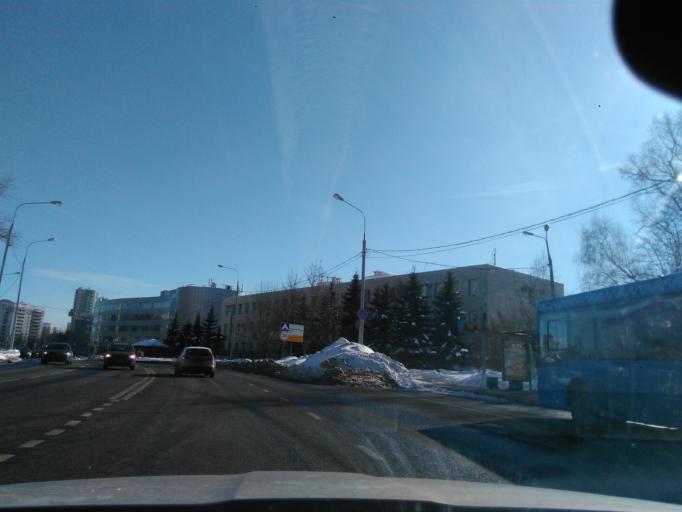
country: RU
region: Moscow
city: Zelenograd
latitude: 55.9851
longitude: 37.1718
